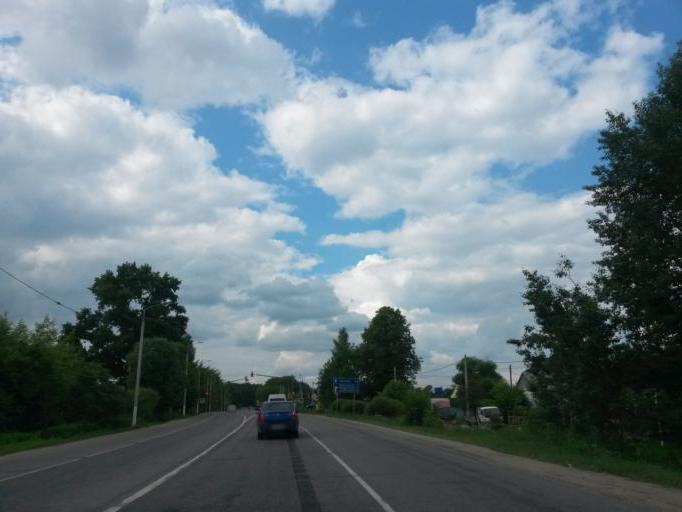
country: RU
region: Moskovskaya
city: Stolbovaya
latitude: 55.2432
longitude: 37.5047
